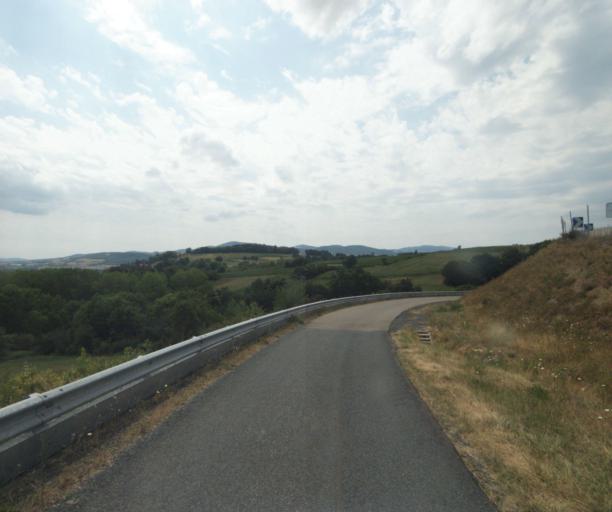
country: FR
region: Rhone-Alpes
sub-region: Departement du Rhone
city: Saint-Germain-Nuelles
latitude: 45.8636
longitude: 4.5983
